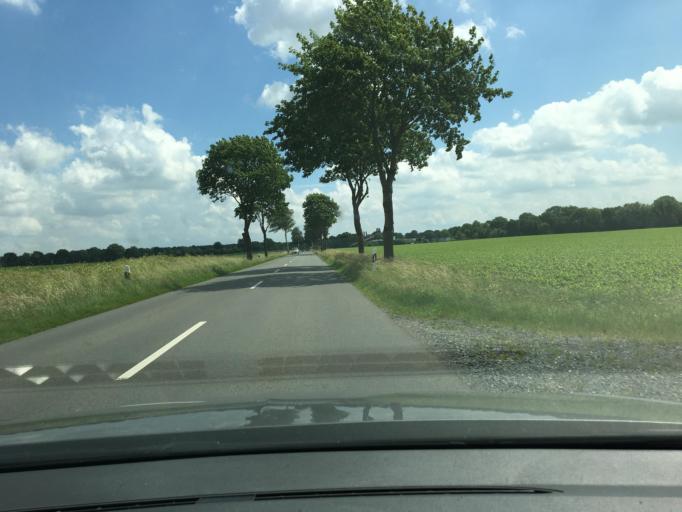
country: DE
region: Lower Saxony
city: Tarmstedt
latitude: 53.2322
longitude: 9.0687
